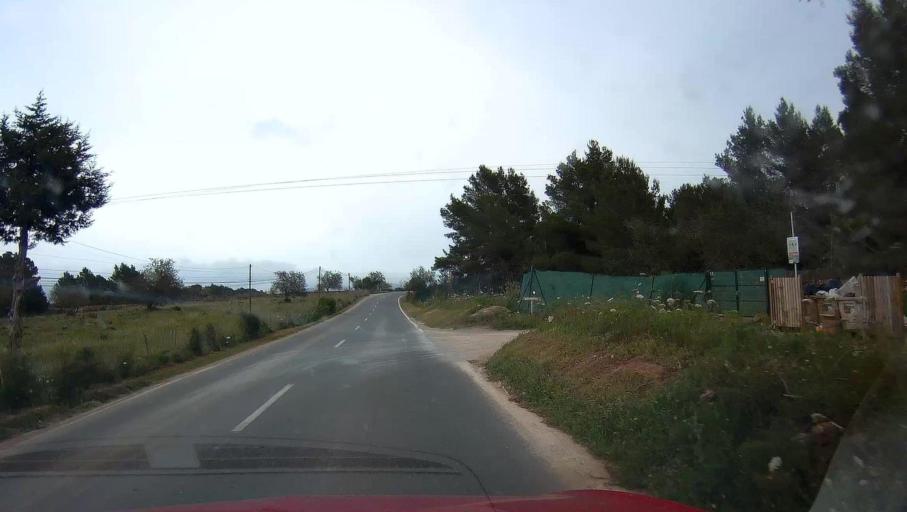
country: ES
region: Balearic Islands
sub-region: Illes Balears
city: Sant Joan de Labritja
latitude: 39.0562
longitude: 1.4504
